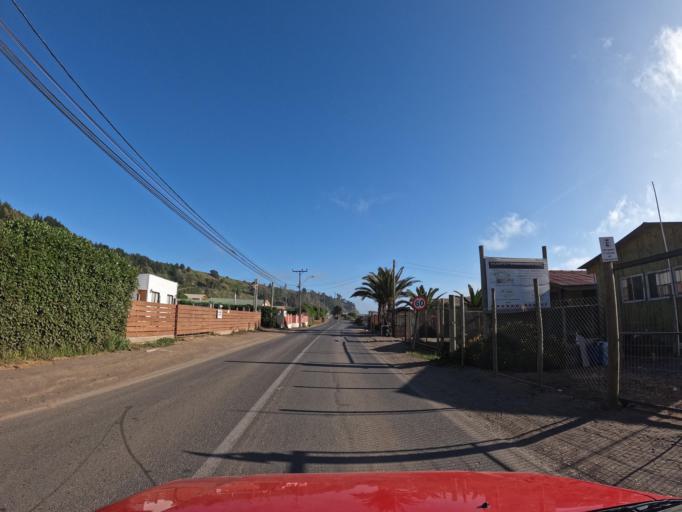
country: CL
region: Maule
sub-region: Provincia de Talca
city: Constitucion
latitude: -34.8993
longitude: -72.1794
